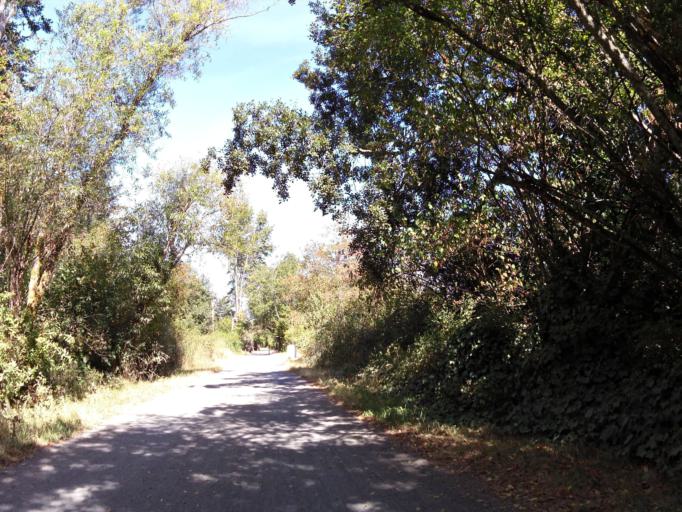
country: CA
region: British Columbia
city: Victoria
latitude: 48.4973
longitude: -123.3604
